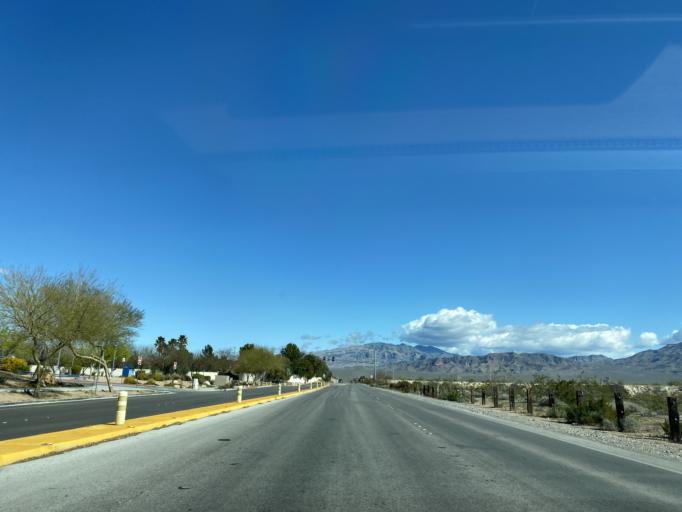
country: US
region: Nevada
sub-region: Clark County
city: North Las Vegas
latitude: 36.3236
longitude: -115.2785
